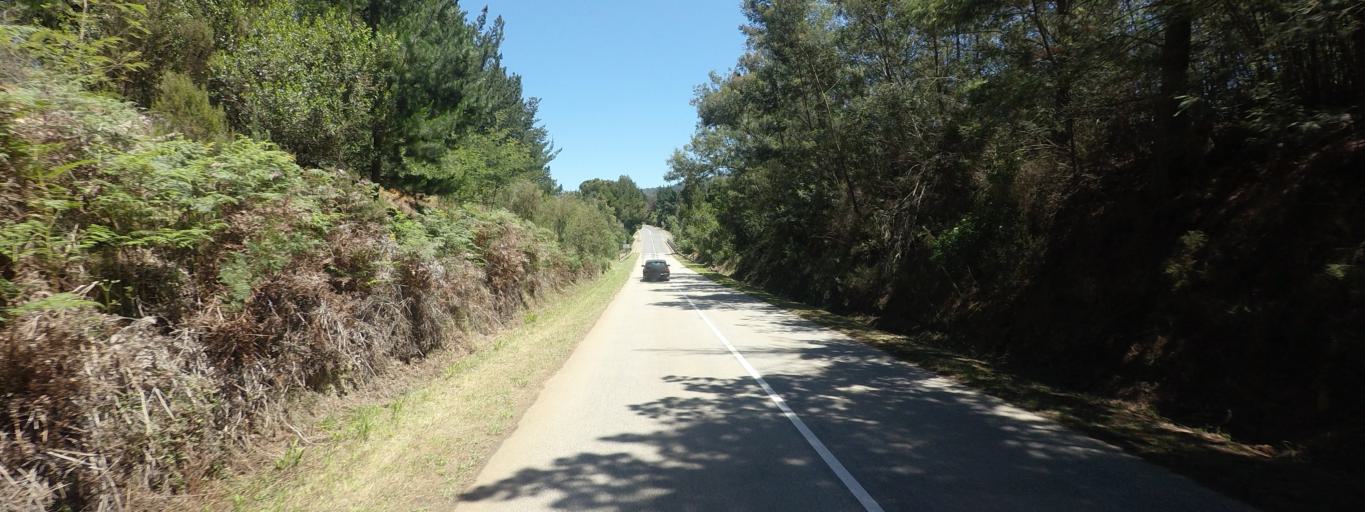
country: ZA
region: Western Cape
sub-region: Eden District Municipality
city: Plettenberg Bay
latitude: -33.9358
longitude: 23.5000
